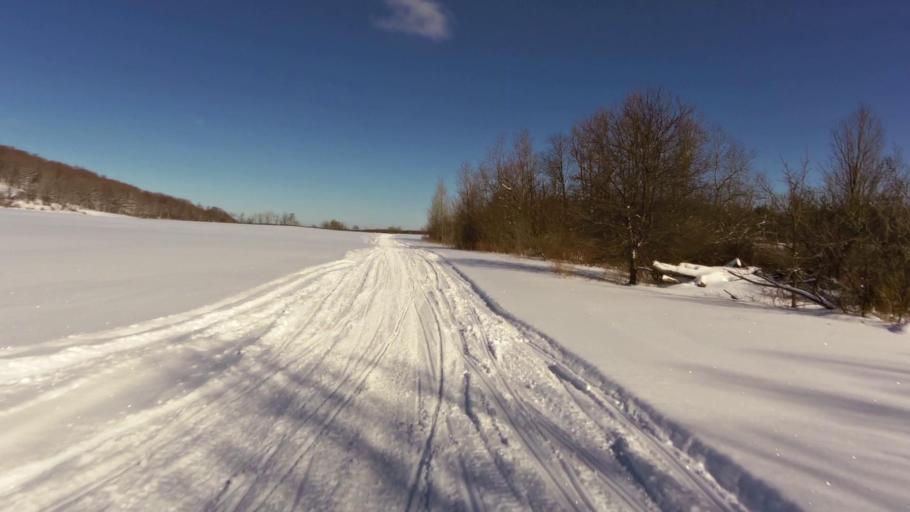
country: US
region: New York
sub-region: Chautauqua County
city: Fredonia
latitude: 42.3622
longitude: -79.1815
